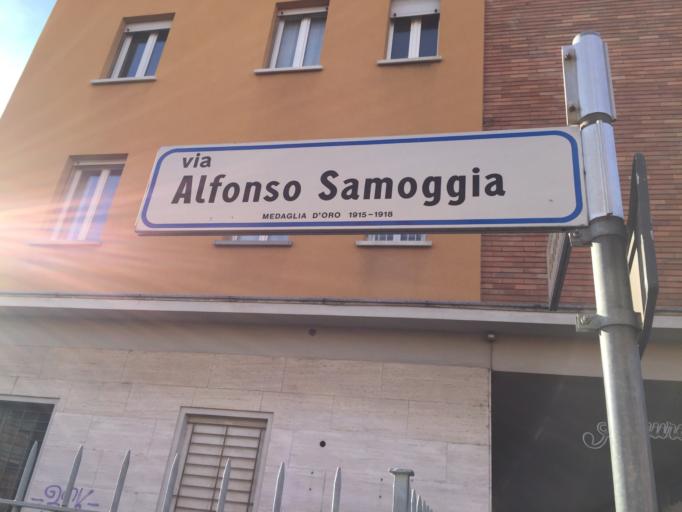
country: IT
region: Emilia-Romagna
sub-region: Provincia di Bologna
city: Casalecchio di Reno
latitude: 44.4966
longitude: 11.2937
